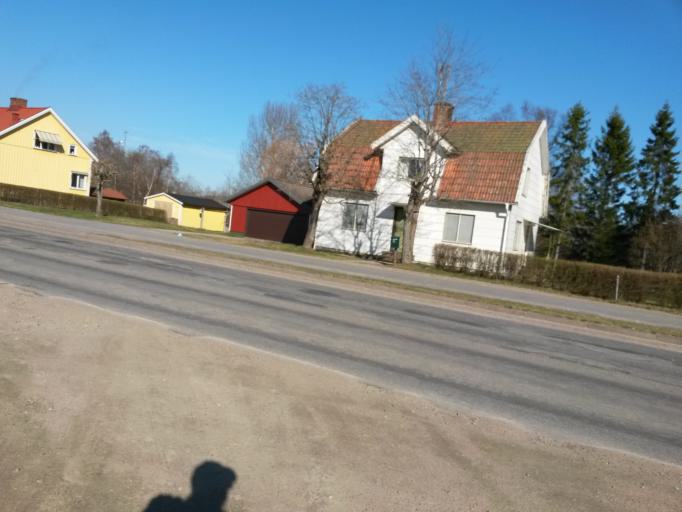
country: SE
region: Vaestra Goetaland
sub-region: Vargarda Kommun
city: Vargarda
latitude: 58.0289
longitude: 12.8201
